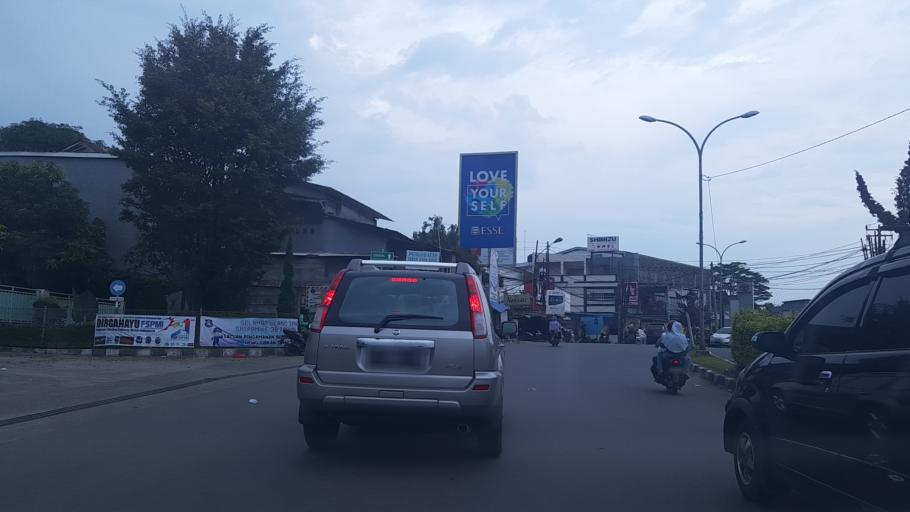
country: ID
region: West Java
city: Citeureup
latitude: -6.4846
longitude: 106.8711
